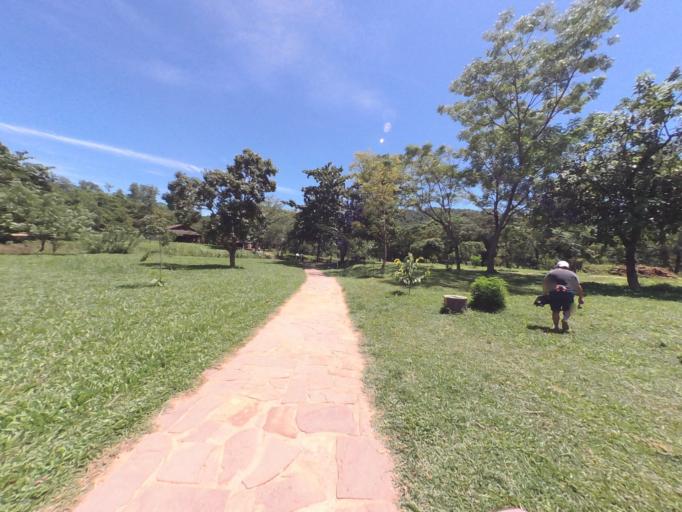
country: VN
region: Quang Nam
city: Dai Loc
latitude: 15.7634
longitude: 108.1239
